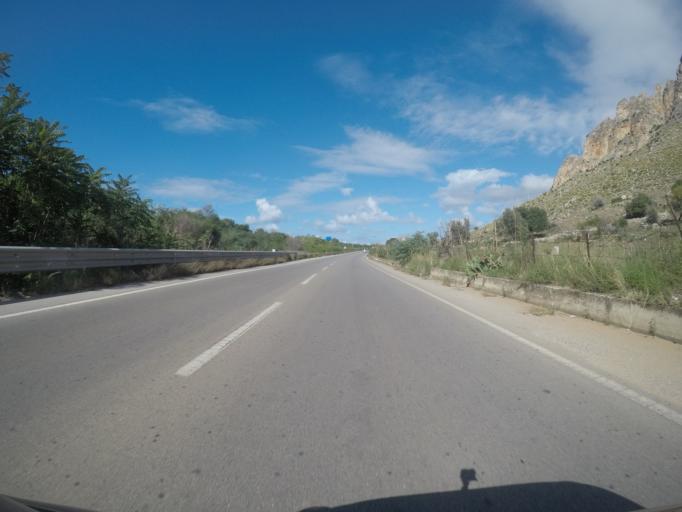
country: IT
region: Sicily
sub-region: Palermo
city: Agliandroni-Paternella
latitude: 38.1324
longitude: 13.0756
